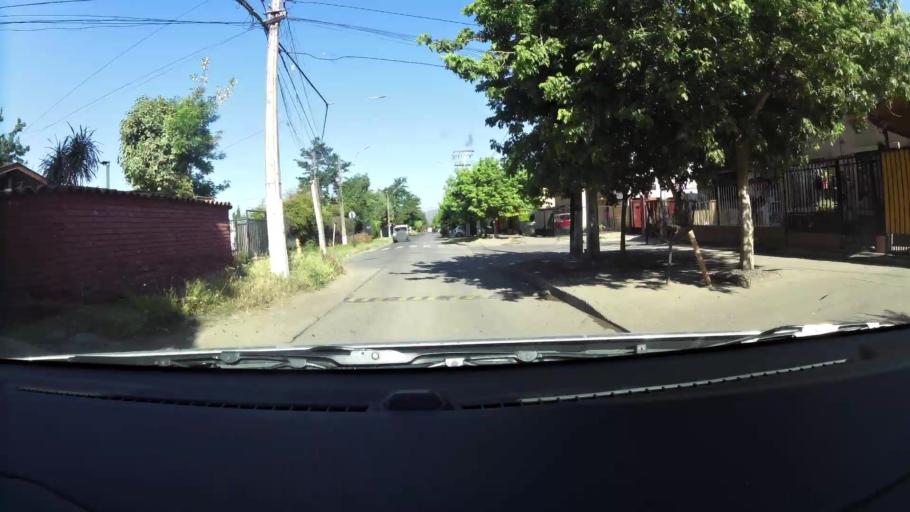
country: CL
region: Santiago Metropolitan
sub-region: Provincia de Maipo
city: San Bernardo
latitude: -33.6188
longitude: -70.6871
